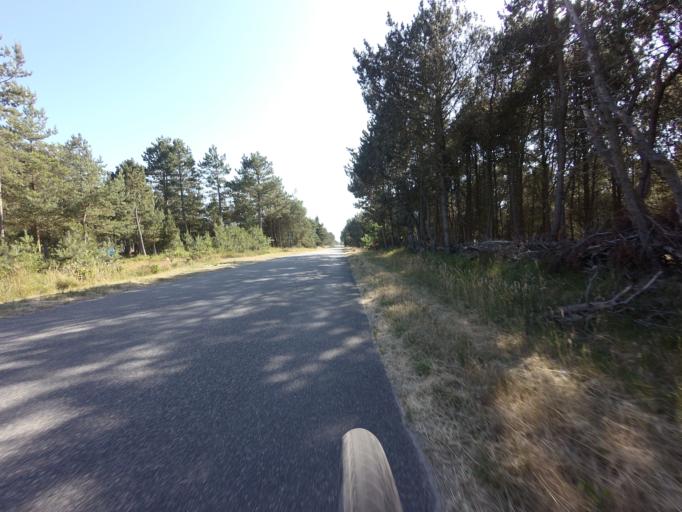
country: DK
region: North Denmark
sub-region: Laeso Kommune
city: Byrum
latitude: 57.2794
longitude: 10.9116
